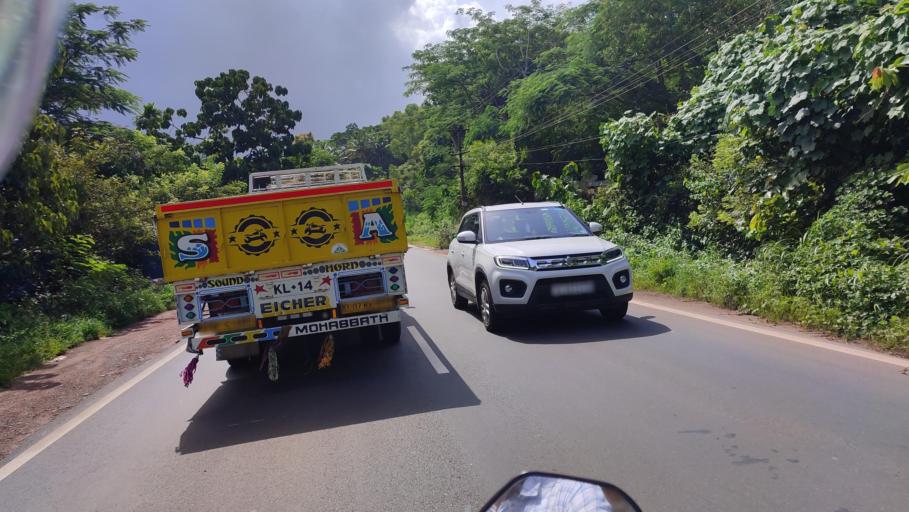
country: IN
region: Kerala
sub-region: Kasaragod District
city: Nileshwar
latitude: 12.2201
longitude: 75.1610
